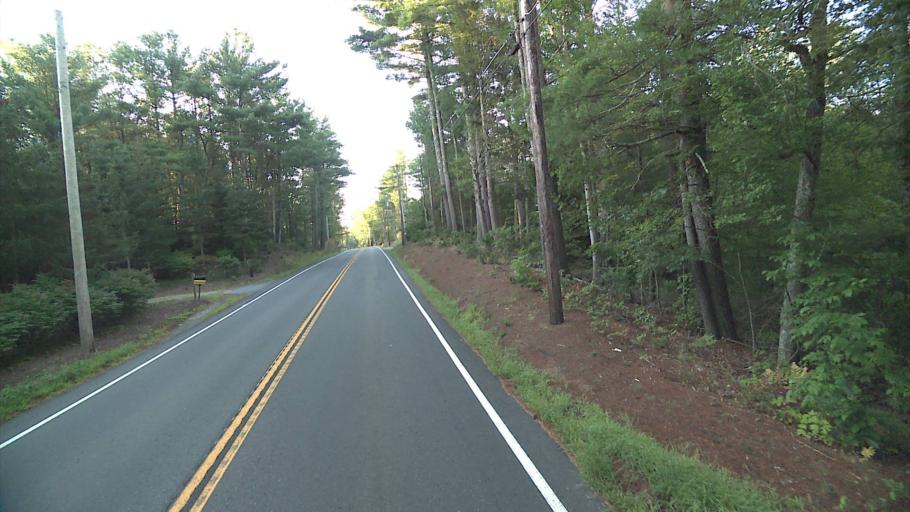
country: US
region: Connecticut
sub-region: Tolland County
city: Stafford
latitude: 42.0243
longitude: -72.3204
